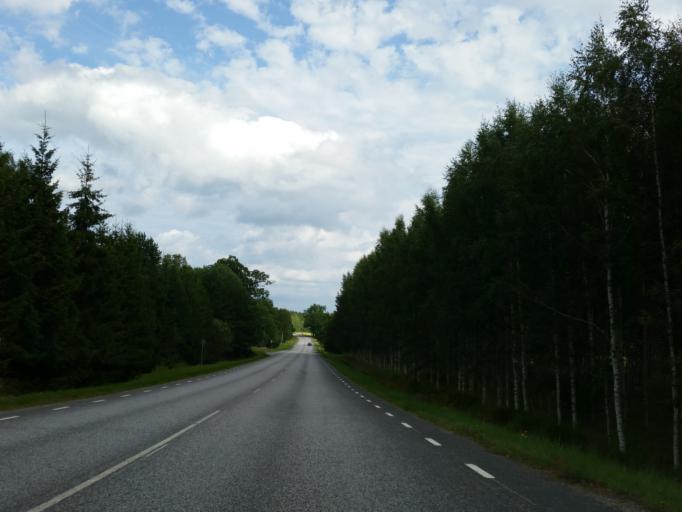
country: SE
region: Soedermanland
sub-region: Strangnas Kommun
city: Mariefred
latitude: 59.2195
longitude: 17.2350
